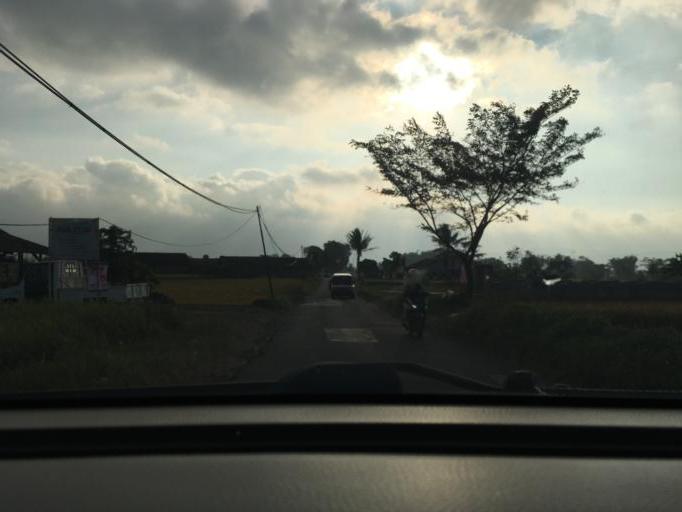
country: ID
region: West Java
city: Rawa
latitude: -7.0329
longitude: 108.3384
